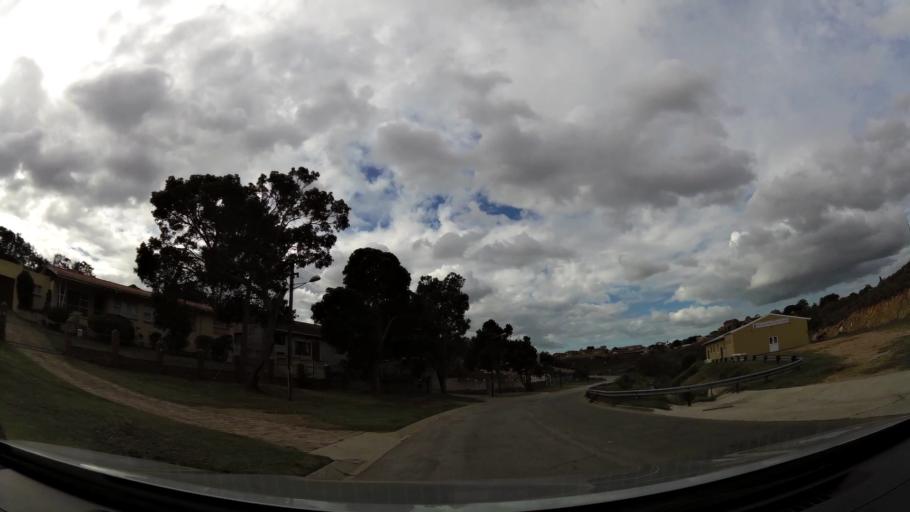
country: ZA
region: Eastern Cape
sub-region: Nelson Mandela Bay Metropolitan Municipality
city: Port Elizabeth
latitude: -33.9363
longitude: 25.5182
